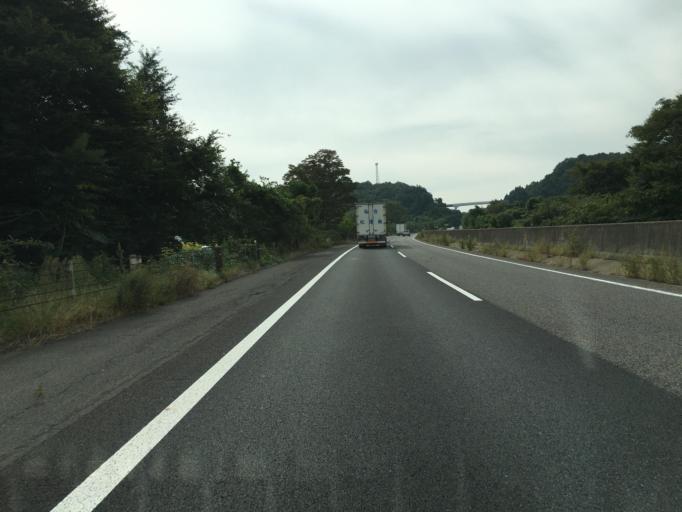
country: JP
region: Fukushima
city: Nihommatsu
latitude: 37.6417
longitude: 140.4356
